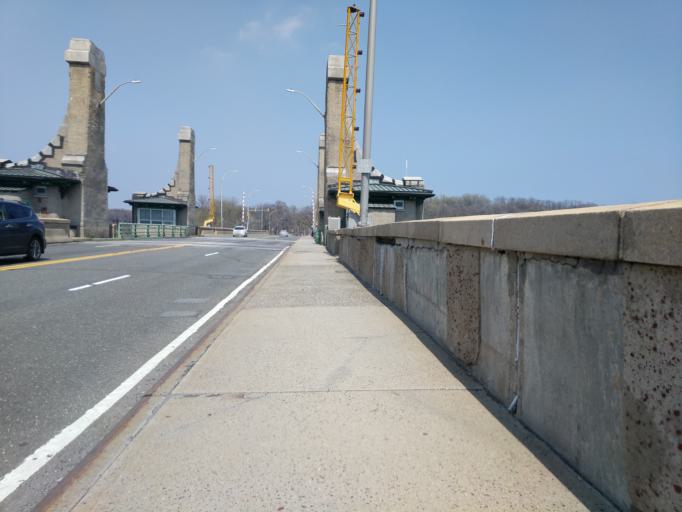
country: US
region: New York
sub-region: Bronx
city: Eastchester
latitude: 40.8616
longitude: -73.8161
